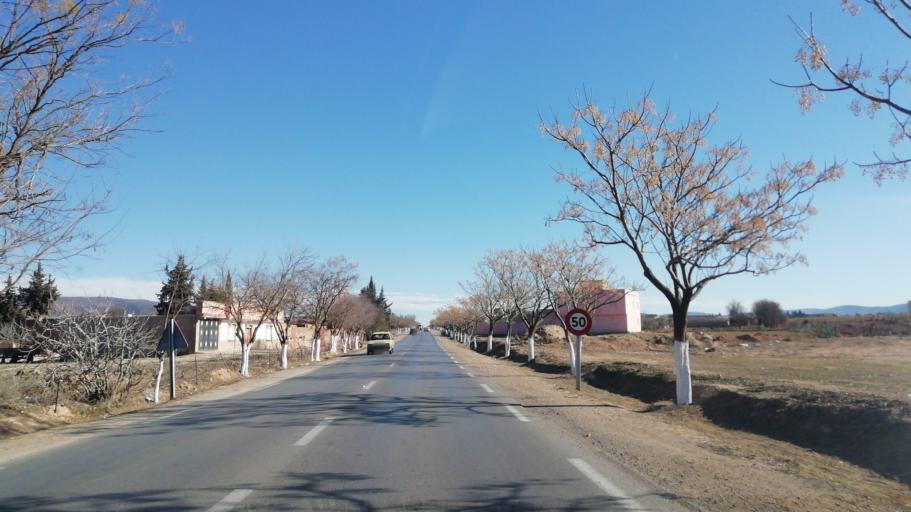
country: DZ
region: Tlemcen
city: Sebdou
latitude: 34.6620
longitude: -1.2941
